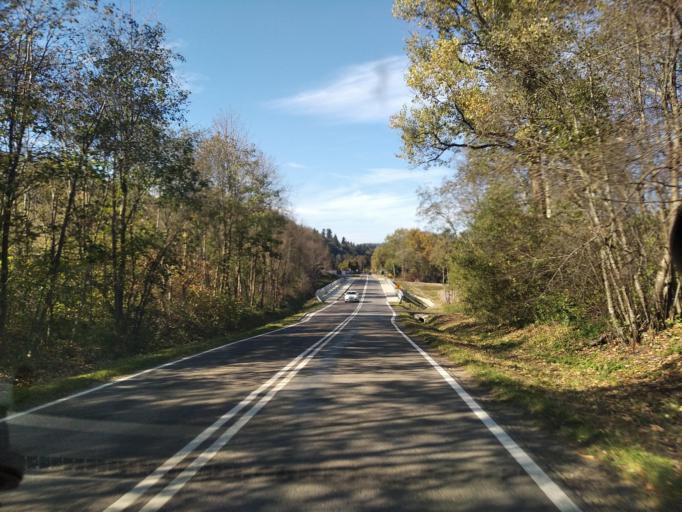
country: PL
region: Subcarpathian Voivodeship
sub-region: Powiat leski
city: Baligrod
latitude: 49.2738
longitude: 22.2872
